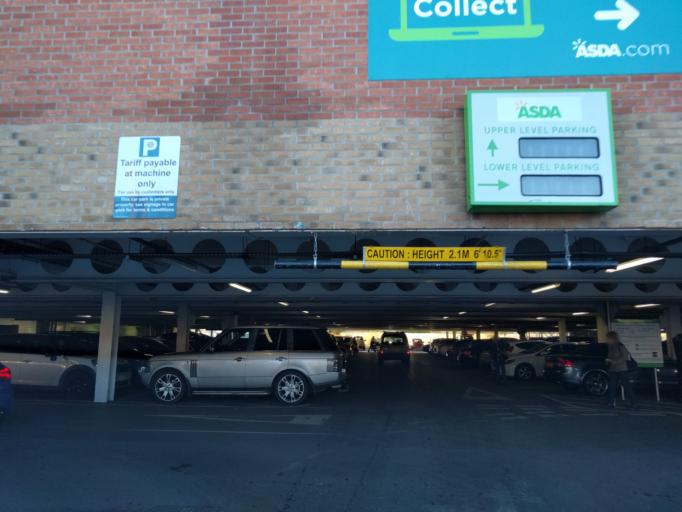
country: GB
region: England
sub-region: Nottinghamshire
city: Newark on Trent
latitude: 53.0748
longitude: -0.8124
